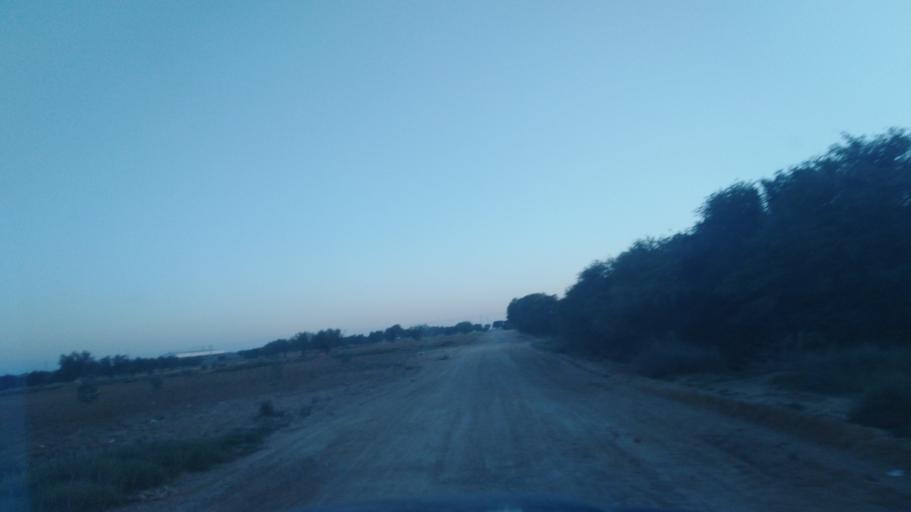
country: TN
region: Safaqis
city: Sfax
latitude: 34.7284
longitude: 10.4463
